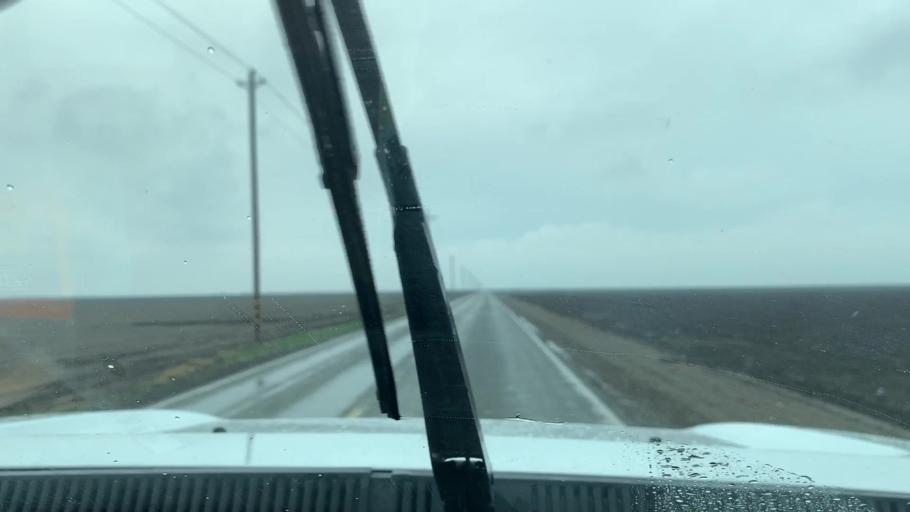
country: US
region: California
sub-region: Tulare County
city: Alpaugh
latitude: 35.9745
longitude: -119.5720
